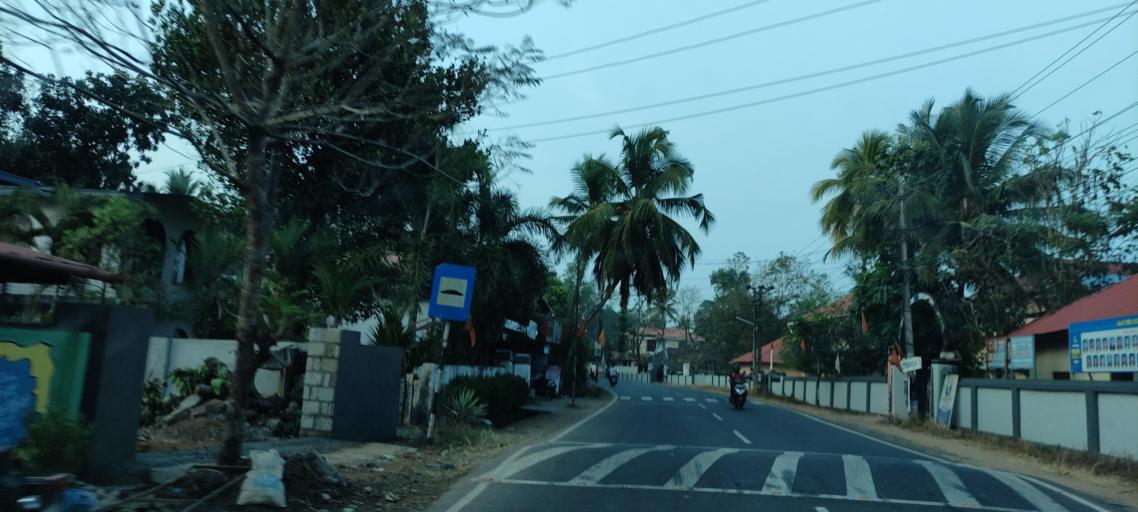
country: IN
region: Kerala
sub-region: Alappuzha
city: Mavelikara
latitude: 9.2810
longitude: 76.5309
